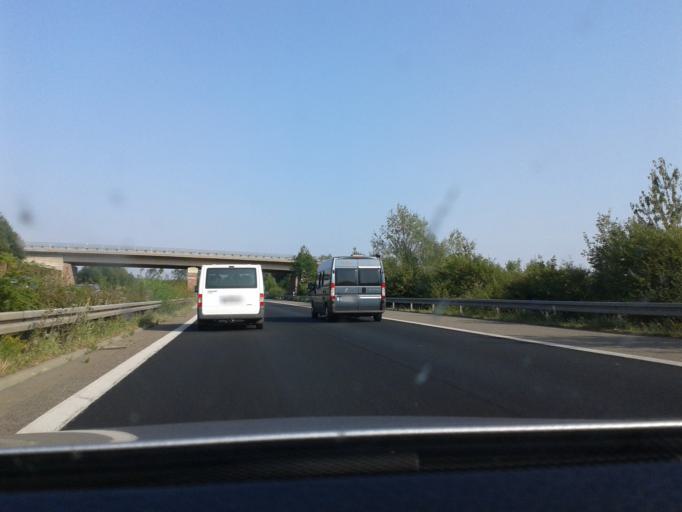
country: DE
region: Saxony-Anhalt
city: Wallhausen
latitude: 51.4548
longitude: 11.1995
